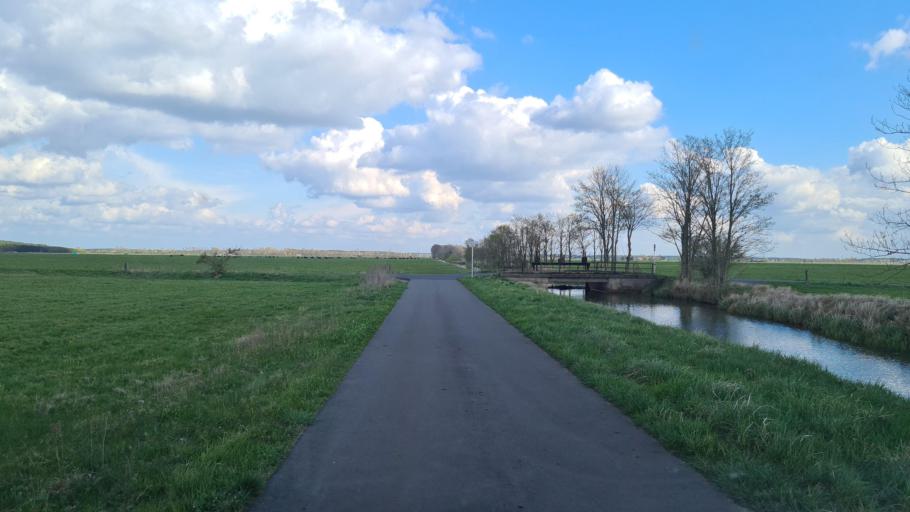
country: DE
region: Brandenburg
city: Herzberg
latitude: 51.7264
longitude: 13.2477
